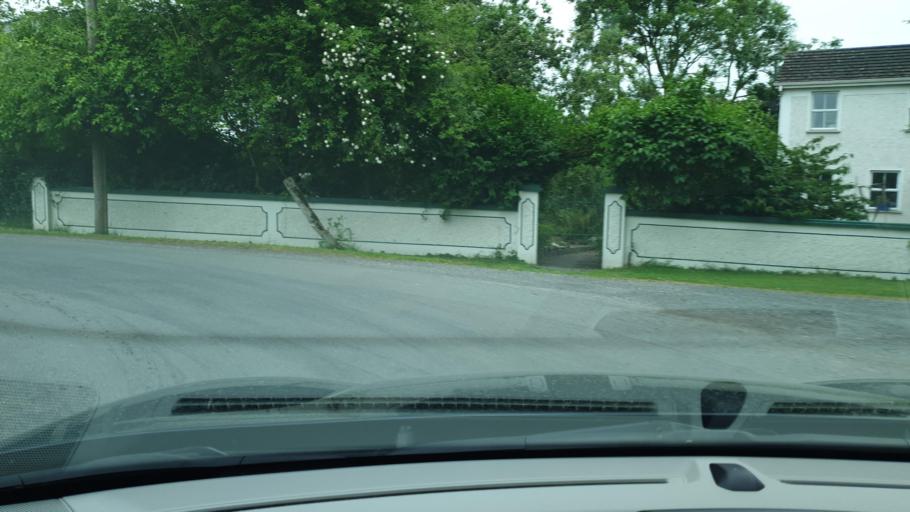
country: IE
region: Leinster
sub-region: An Mhi
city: Ashbourne
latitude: 53.4802
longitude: -6.4042
